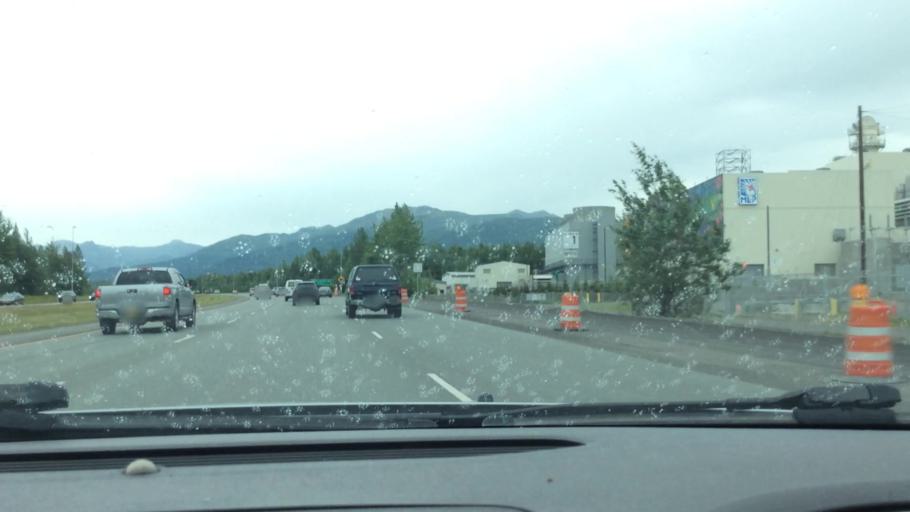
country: US
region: Alaska
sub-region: Anchorage Municipality
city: Elmendorf Air Force Base
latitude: 61.2304
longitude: -149.7171
